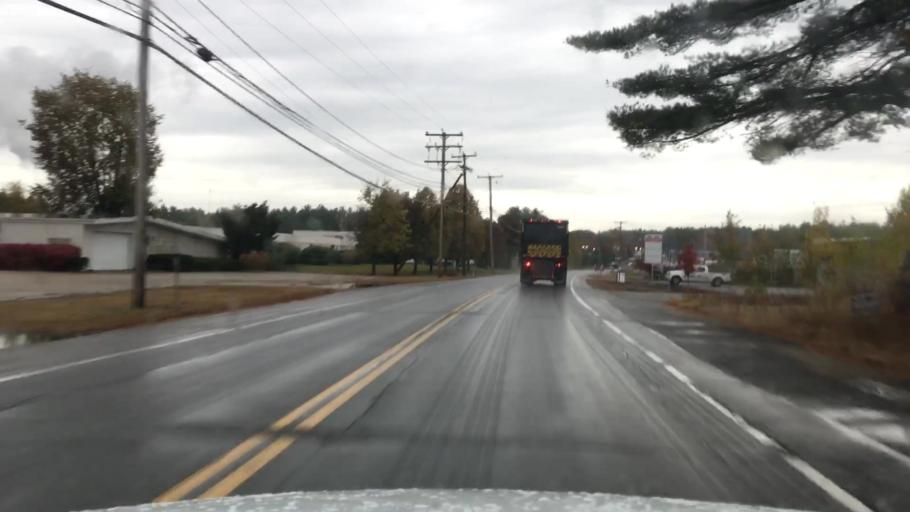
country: US
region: New Hampshire
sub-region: Strafford County
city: Somersworth
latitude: 43.2600
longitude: -70.9040
